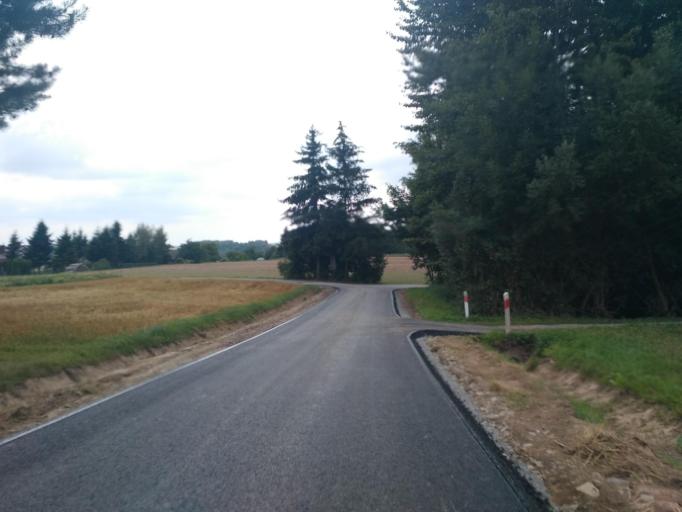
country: PL
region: Subcarpathian Voivodeship
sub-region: Powiat rzeszowski
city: Chmielnik
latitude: 50.0026
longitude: 22.1391
